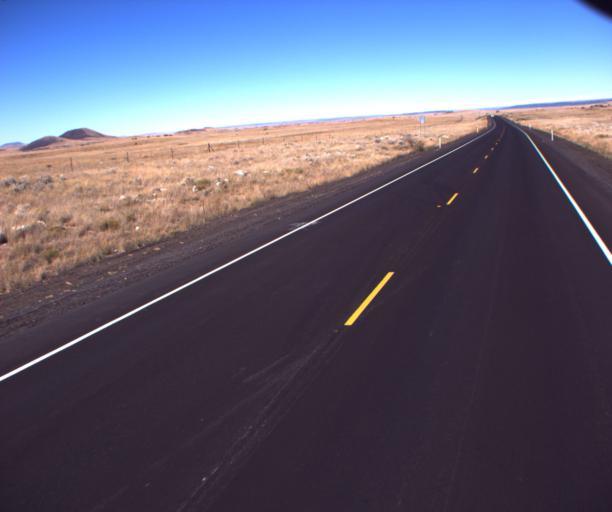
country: US
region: Arizona
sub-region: Apache County
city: Springerville
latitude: 34.1860
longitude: -109.3197
